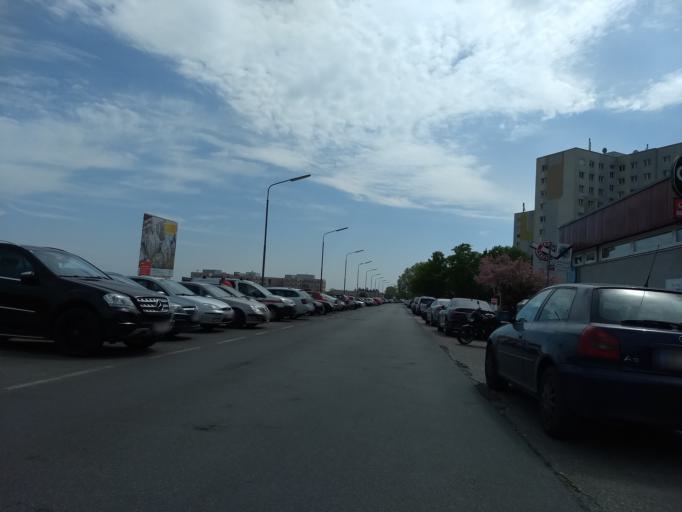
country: AT
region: Lower Austria
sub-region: Politischer Bezirk Wien-Umgebung
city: Gerasdorf bei Wien
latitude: 48.2422
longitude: 16.4825
